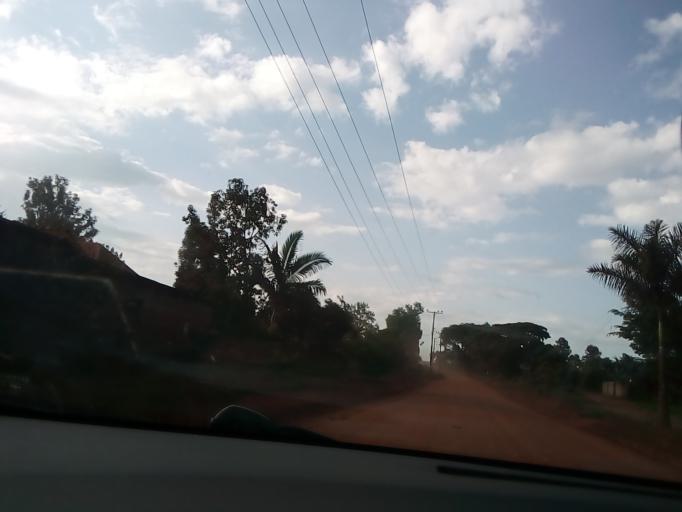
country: UG
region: Central Region
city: Masaka
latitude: -0.3553
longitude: 31.7421
